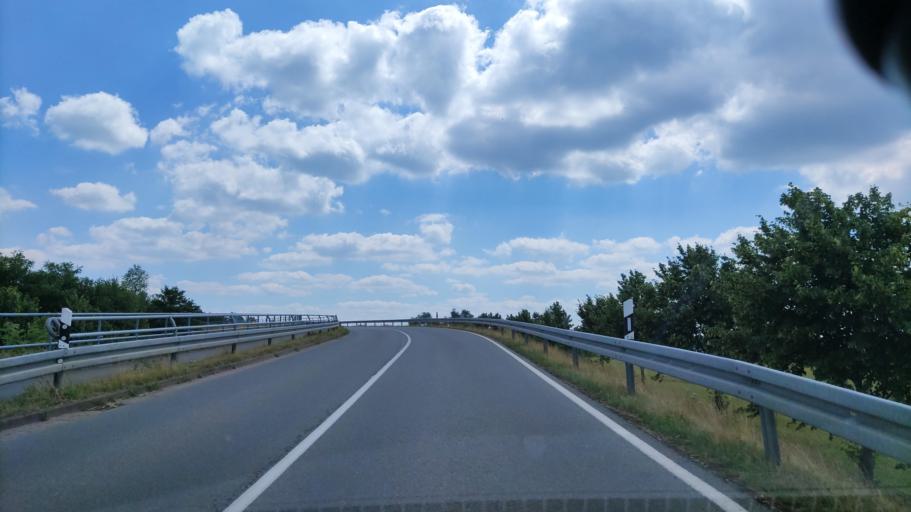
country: DE
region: Mecklenburg-Vorpommern
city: Hagenow
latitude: 53.3739
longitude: 11.1444
